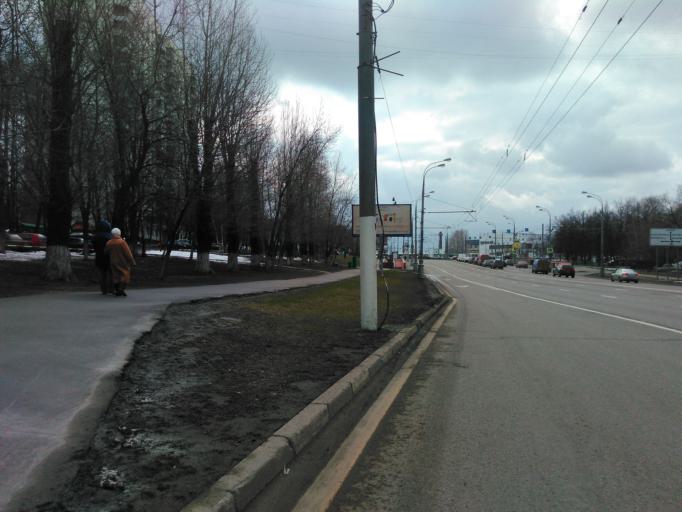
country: RU
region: Moscow
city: Zyuzino
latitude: 55.6514
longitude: 37.5658
